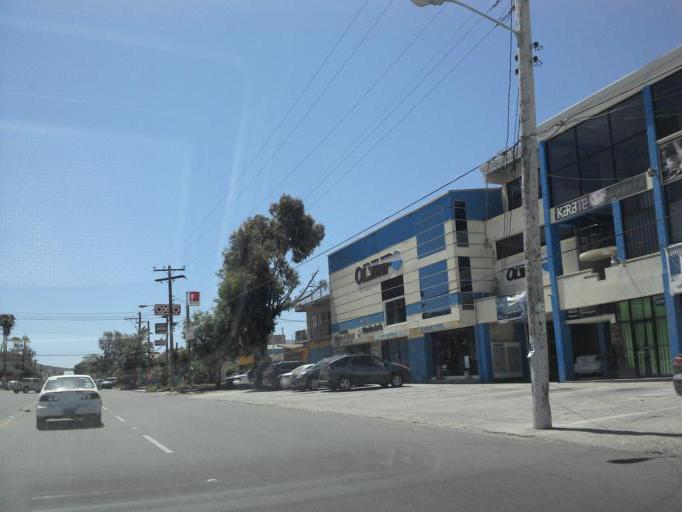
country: MX
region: Baja California
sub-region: Tijuana
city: La Esperanza [Granjas Familiares]
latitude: 32.5171
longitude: -117.1162
